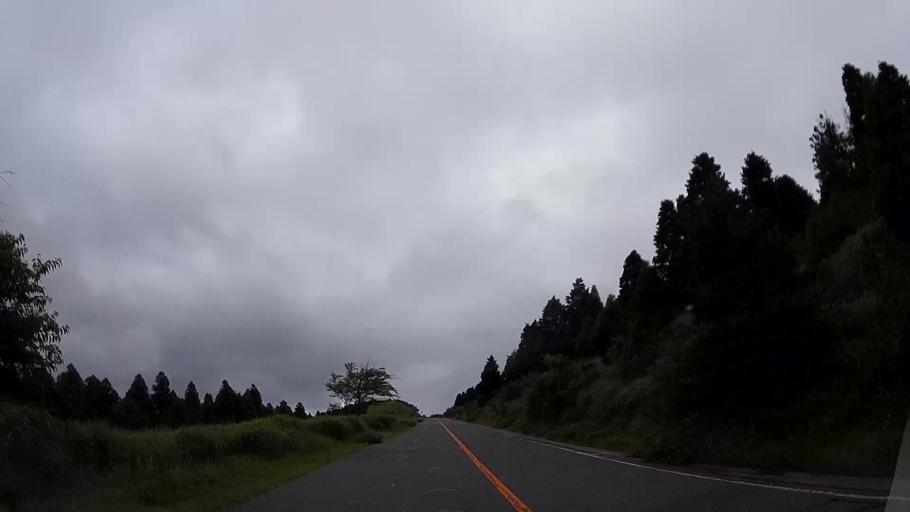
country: JP
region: Kumamoto
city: Aso
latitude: 32.8868
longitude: 131.0553
